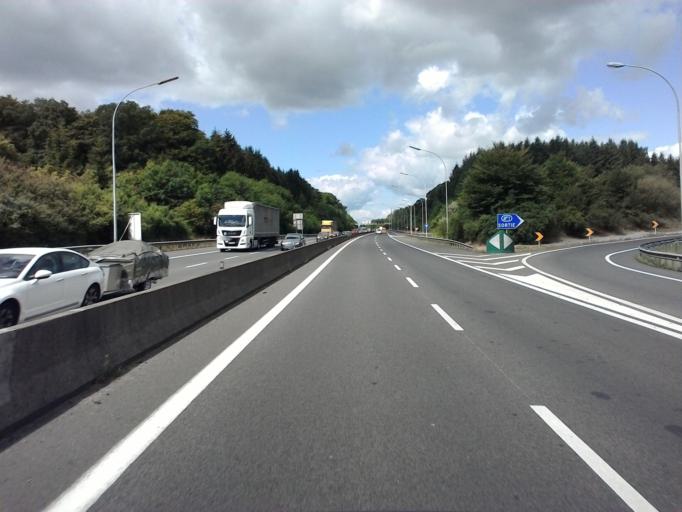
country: LU
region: Luxembourg
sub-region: Canton de Capellen
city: Garnich
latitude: 49.6356
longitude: 5.9538
